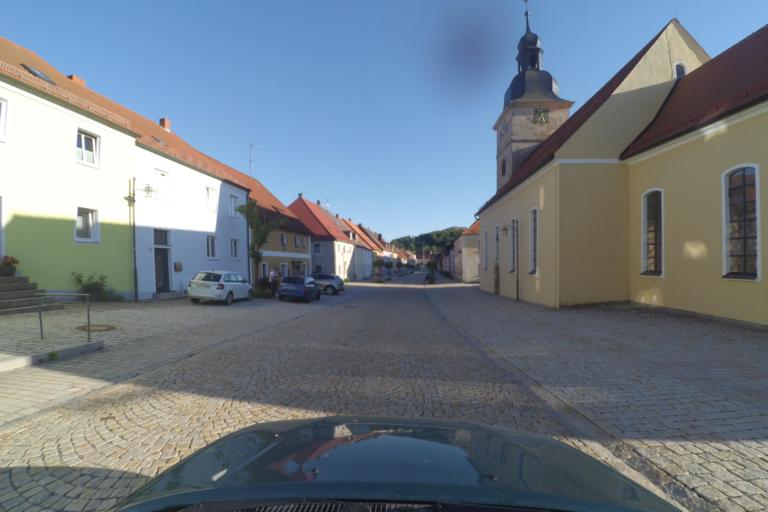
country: DE
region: Bavaria
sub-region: Upper Palatinate
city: Kastl
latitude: 49.8654
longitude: 11.9518
